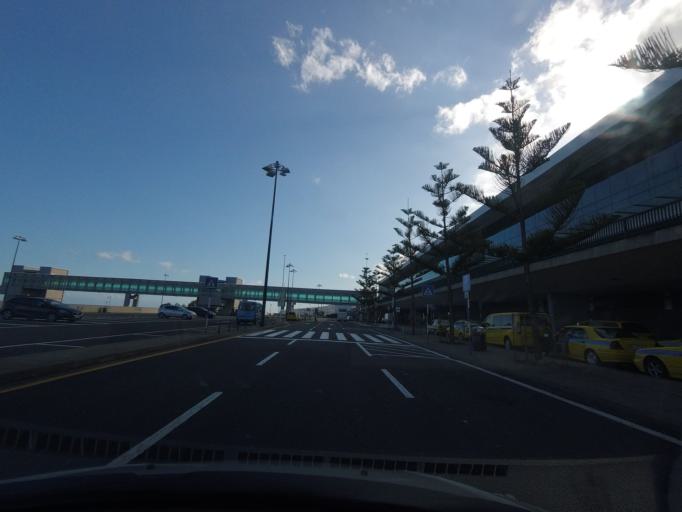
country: PT
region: Madeira
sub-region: Machico
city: Machico
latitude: 32.6934
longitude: -16.7749
